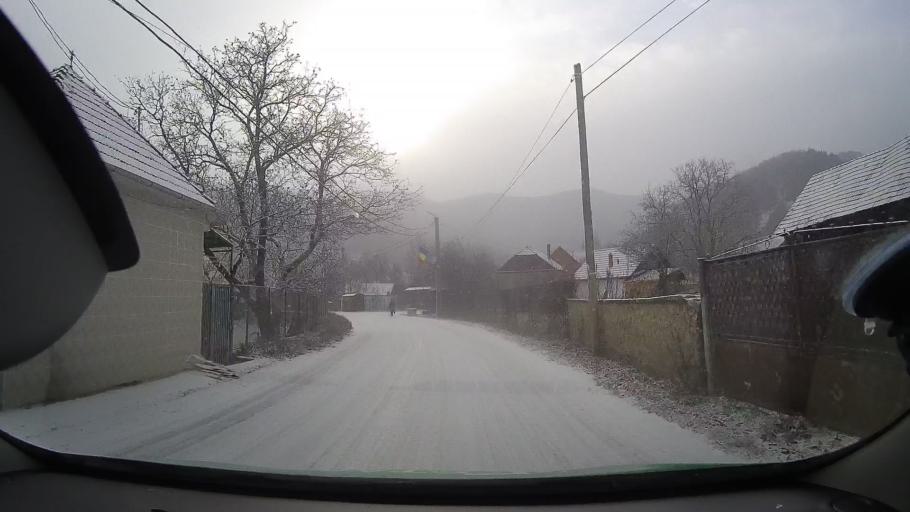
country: RO
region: Alba
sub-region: Comuna Rimetea
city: Rimetea
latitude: 46.3882
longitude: 23.5621
